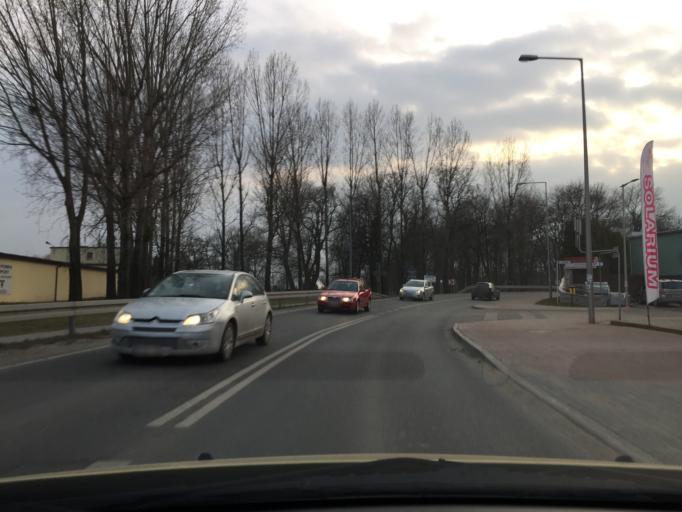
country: PL
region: Greater Poland Voivodeship
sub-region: Powiat poznanski
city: Plewiska
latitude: 52.3881
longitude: 16.7865
